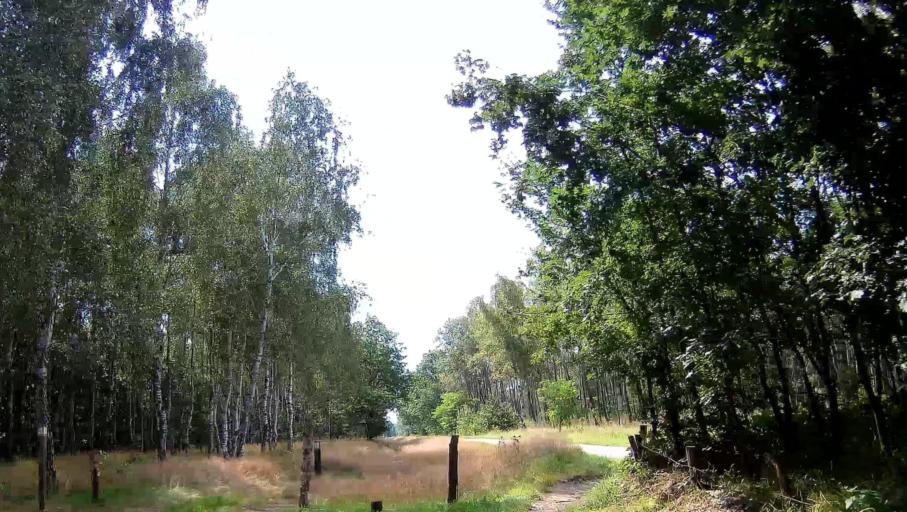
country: BE
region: Flanders
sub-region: Provincie Limburg
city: Lommel
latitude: 51.2247
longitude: 5.2443
